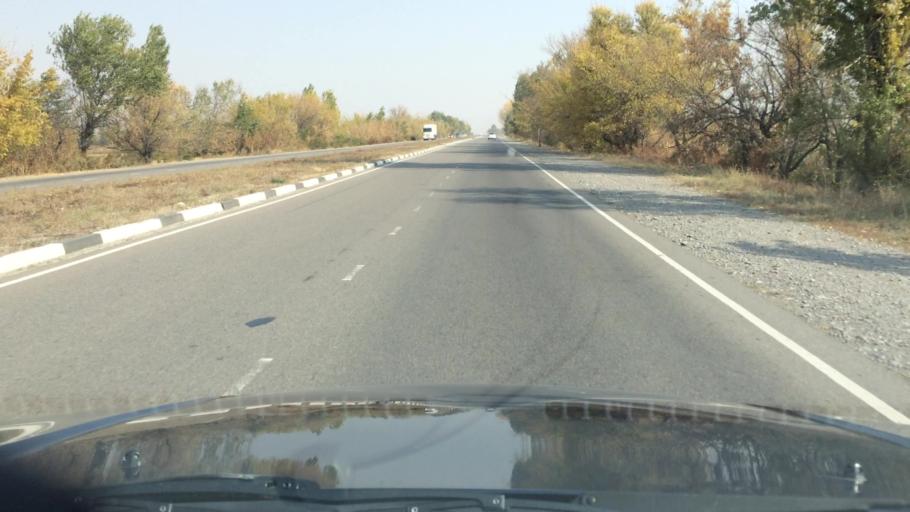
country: KG
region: Chuy
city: Kant
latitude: 42.9516
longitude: 74.7877
